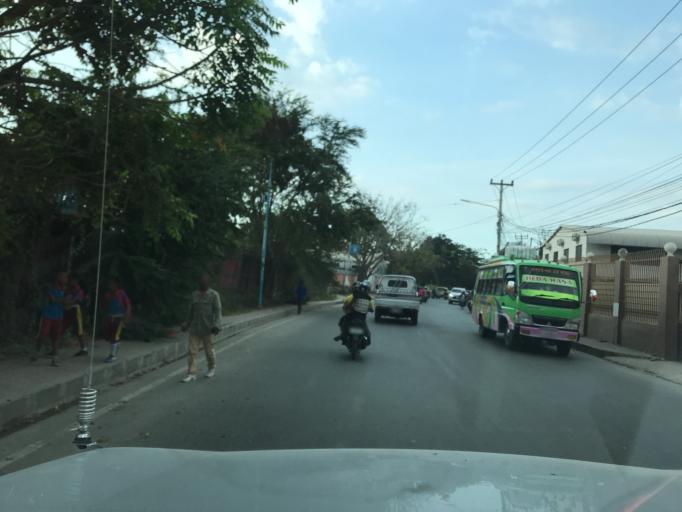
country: TL
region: Dili
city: Dili
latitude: -8.5487
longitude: 125.5434
